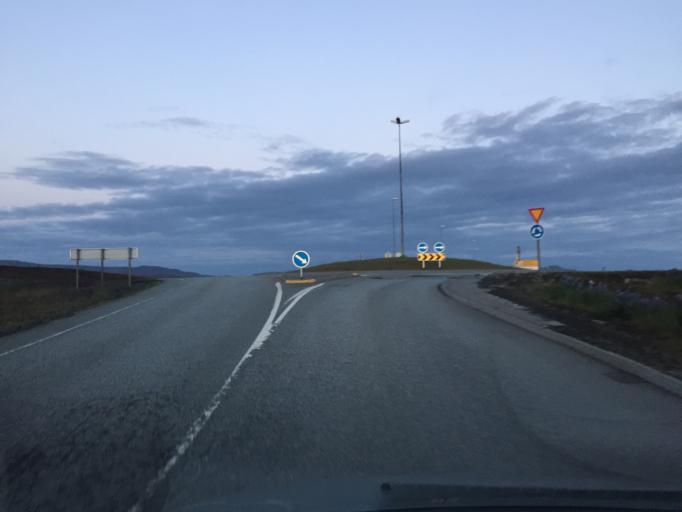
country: IS
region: Southern Peninsula
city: Vogar
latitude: 63.9620
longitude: -22.4203
